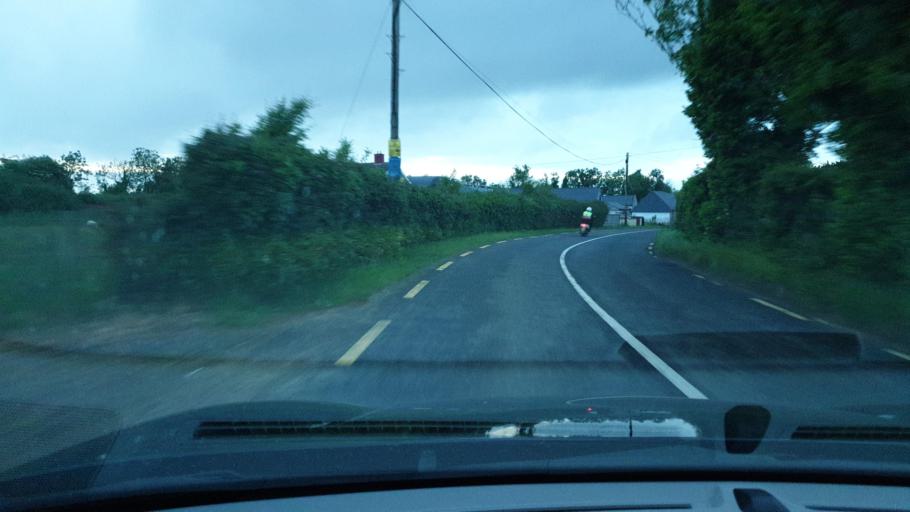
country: IE
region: Leinster
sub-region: An Mhi
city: Ashbourne
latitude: 53.5115
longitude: -6.3197
